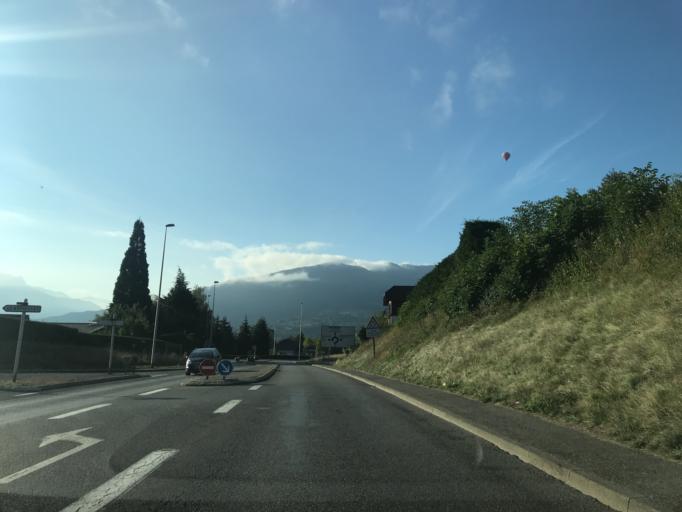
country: FR
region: Rhone-Alpes
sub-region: Departement de la Haute-Savoie
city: Sevrier
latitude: 45.8469
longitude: 6.1469
